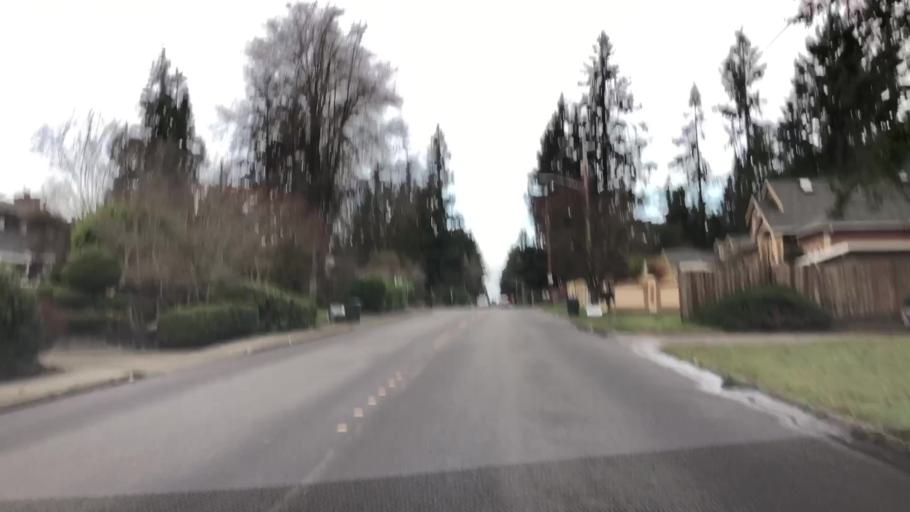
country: US
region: Washington
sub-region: King County
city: West Lake Sammamish
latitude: 47.6110
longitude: -122.1214
